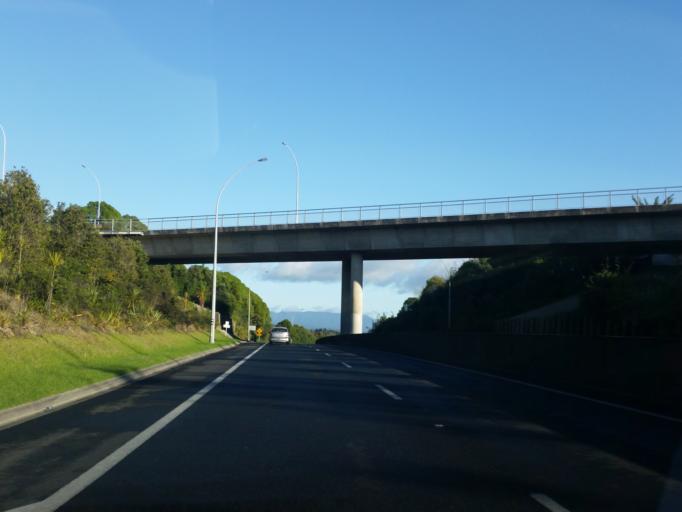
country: NZ
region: Bay of Plenty
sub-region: Tauranga City
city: Tauranga
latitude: -37.6996
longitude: 176.1327
